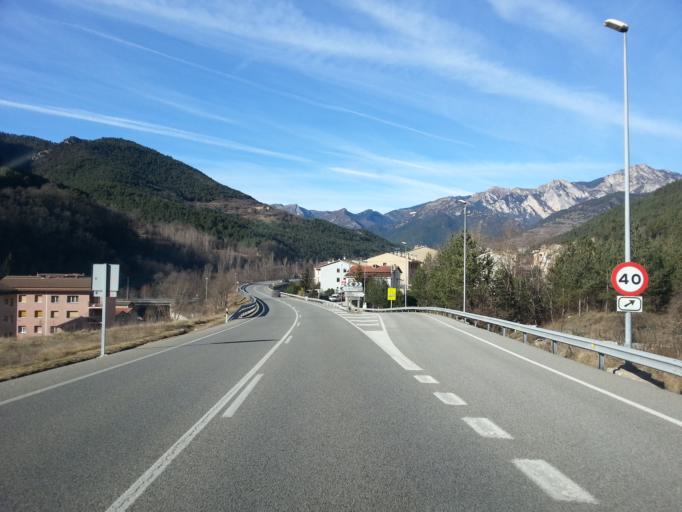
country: ES
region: Catalonia
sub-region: Provincia de Barcelona
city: Guardiola de Bergueda
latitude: 42.2358
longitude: 1.8785
